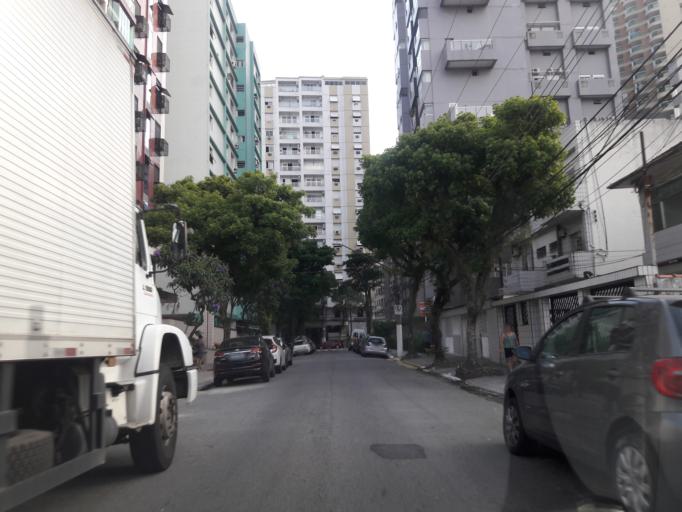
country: BR
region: Sao Paulo
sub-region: Santos
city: Santos
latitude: -23.9658
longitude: -46.3411
